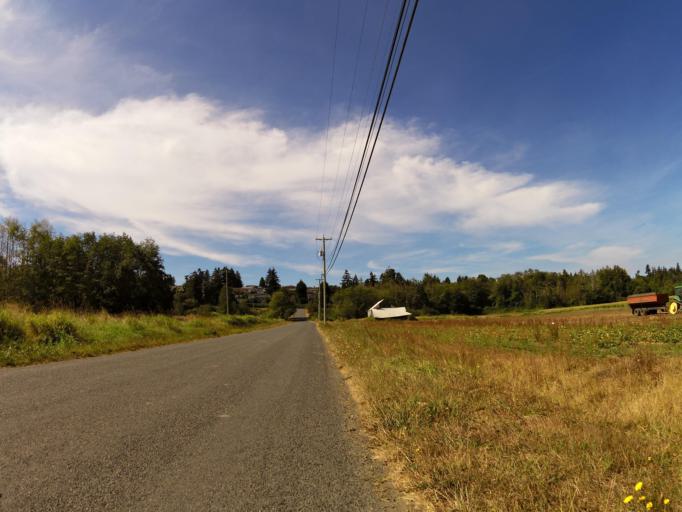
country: CA
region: British Columbia
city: North Saanich
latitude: 48.5616
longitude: -123.3905
